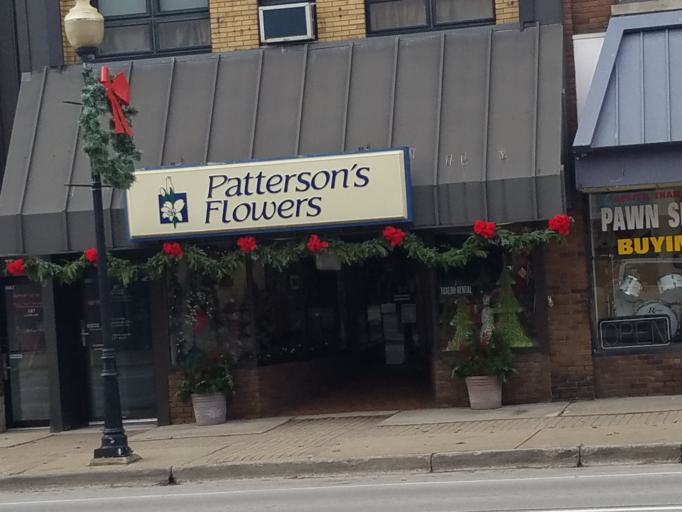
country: US
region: Michigan
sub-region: Wexford County
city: Cadillac
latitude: 44.2506
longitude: -85.3997
